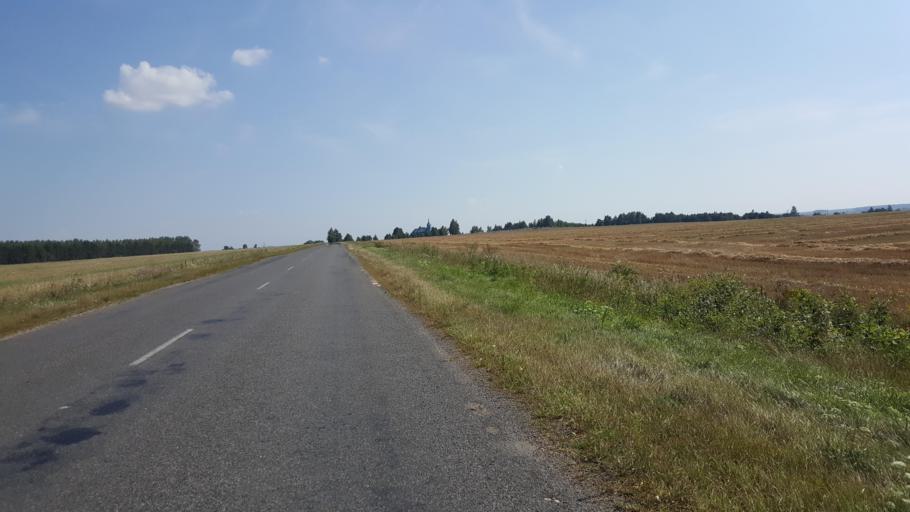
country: BY
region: Brest
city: Kamyanyets
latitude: 52.4514
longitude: 23.7295
